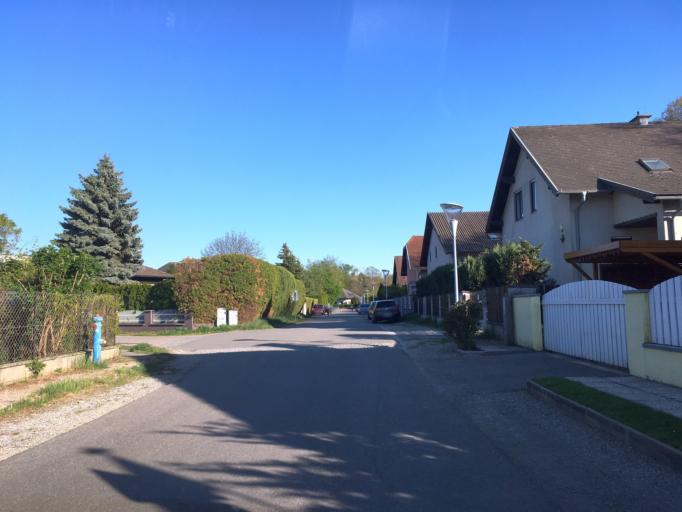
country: AT
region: Lower Austria
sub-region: Politischer Bezirk Ganserndorf
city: Strasshof an der Nordbahn
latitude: 48.3286
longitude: 16.6703
